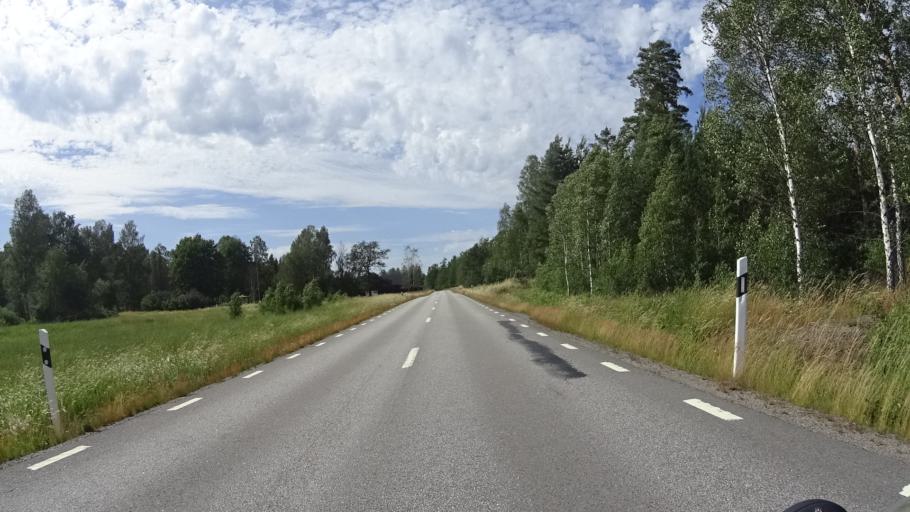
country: SE
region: OEstergoetland
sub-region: Atvidabergs Kommun
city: Atvidaberg
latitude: 58.0896
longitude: 16.1382
